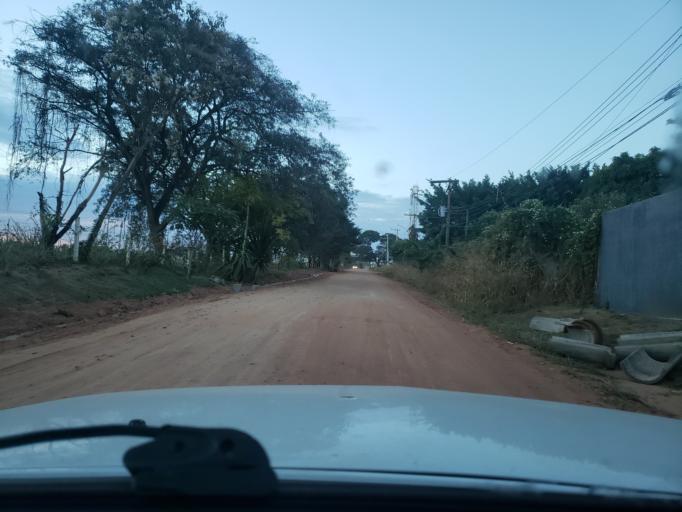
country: BR
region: Sao Paulo
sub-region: Mogi-Mirim
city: Mogi Mirim
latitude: -22.4939
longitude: -46.9821
